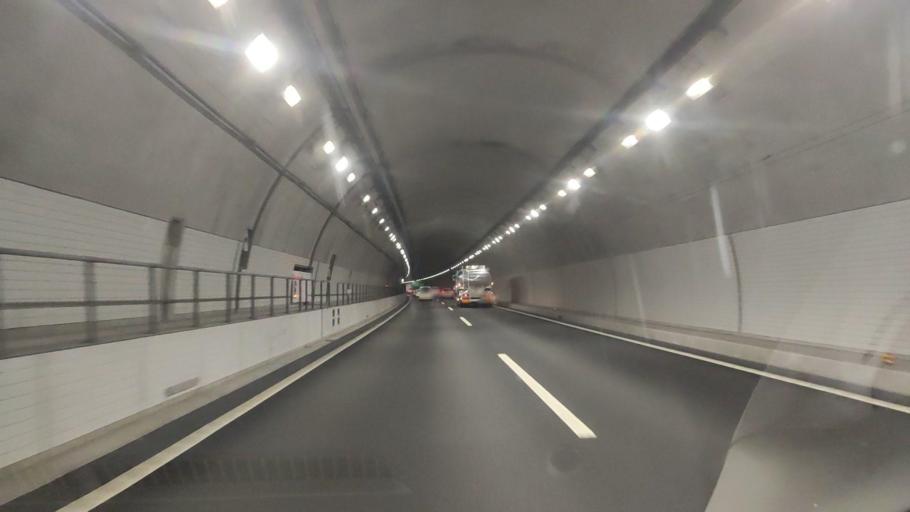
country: JP
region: Kanagawa
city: Zama
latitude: 35.5352
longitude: 139.3276
